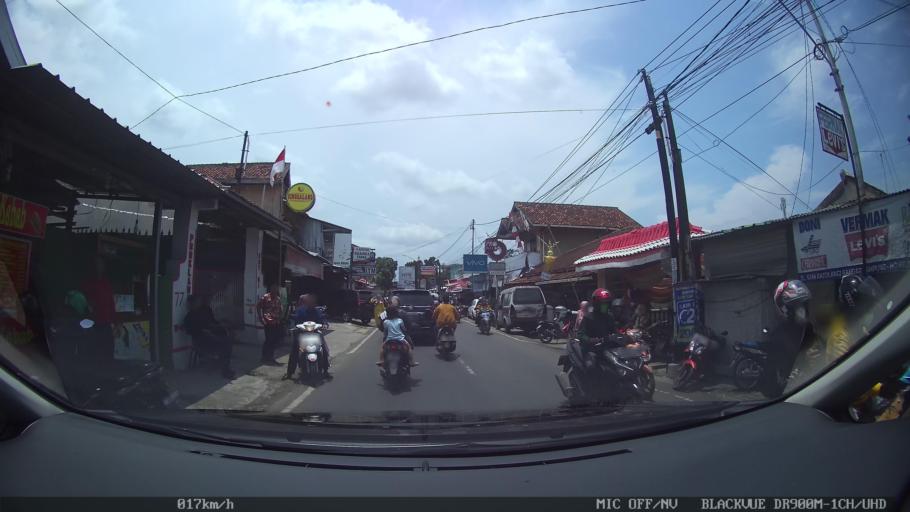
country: ID
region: Lampung
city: Kedaton
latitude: -5.3975
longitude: 105.2487
